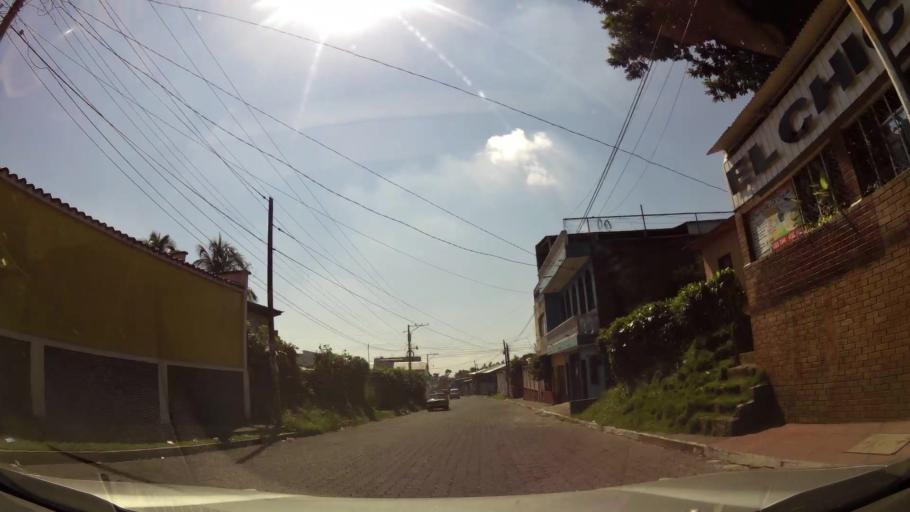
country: GT
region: Suchitepeque
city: Mazatenango
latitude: 14.5327
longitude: -91.4981
